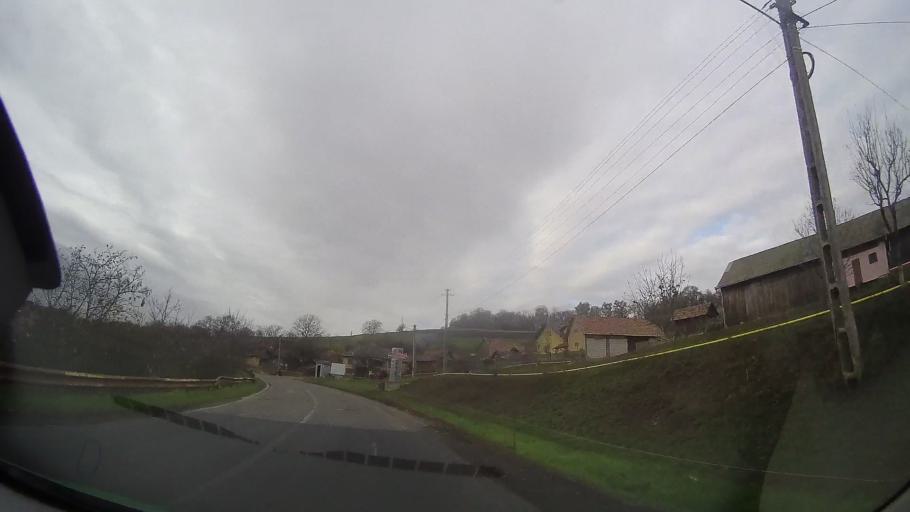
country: RO
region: Bistrita-Nasaud
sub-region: Comuna Silvasu de Campie
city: Silvasu de Campie
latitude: 46.7781
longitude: 24.3179
